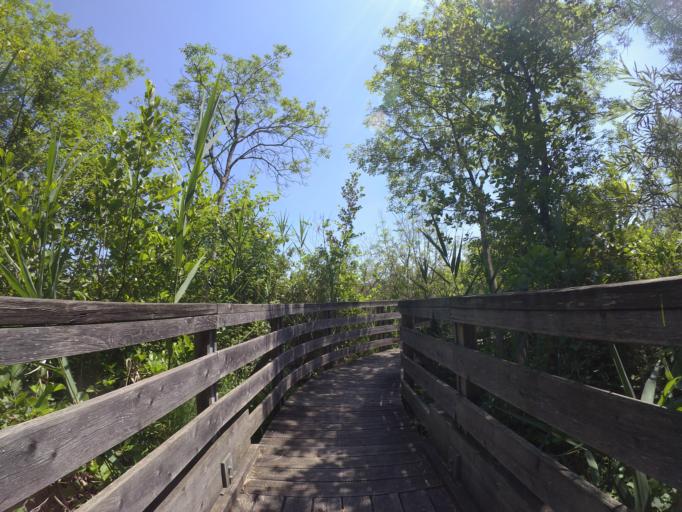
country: IT
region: Friuli Venezia Giulia
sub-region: Provincia di Udine
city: Bertiolo
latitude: 45.9194
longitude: 13.0757
